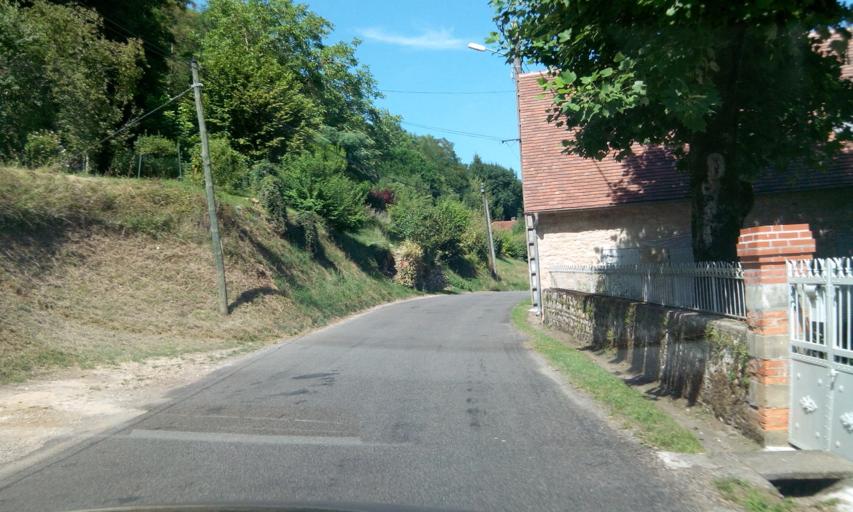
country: FR
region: Midi-Pyrenees
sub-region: Departement du Lot
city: Vayrac
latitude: 44.9353
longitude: 1.6564
